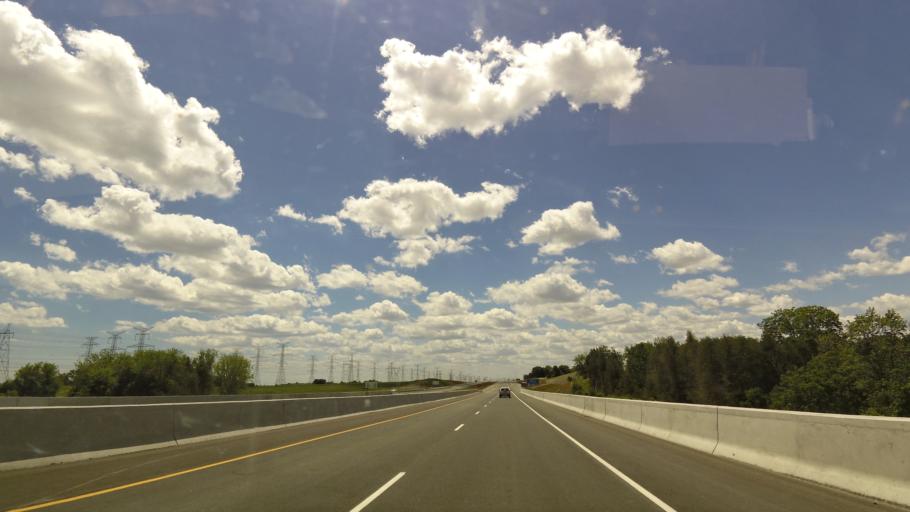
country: CA
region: Ontario
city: Oshawa
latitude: 43.9598
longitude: -78.9261
